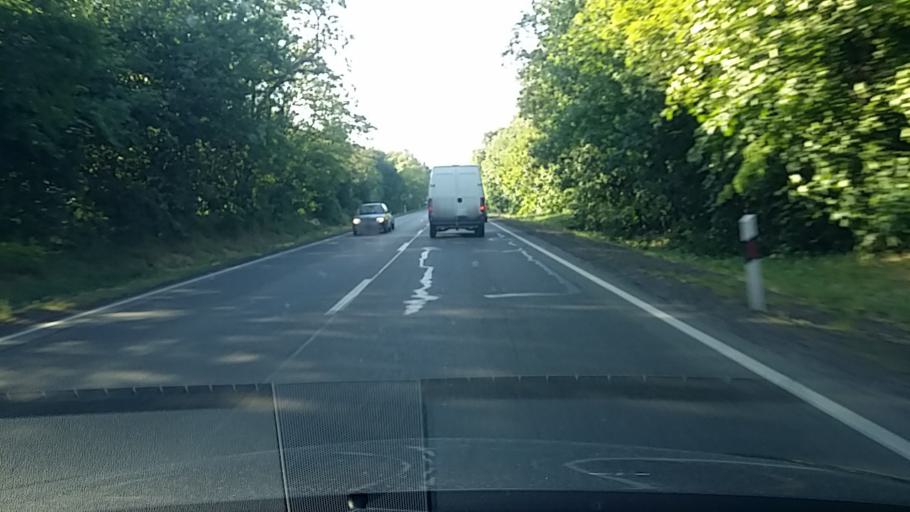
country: HU
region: Fejer
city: dunaujvaros
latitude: 46.9367
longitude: 18.9223
